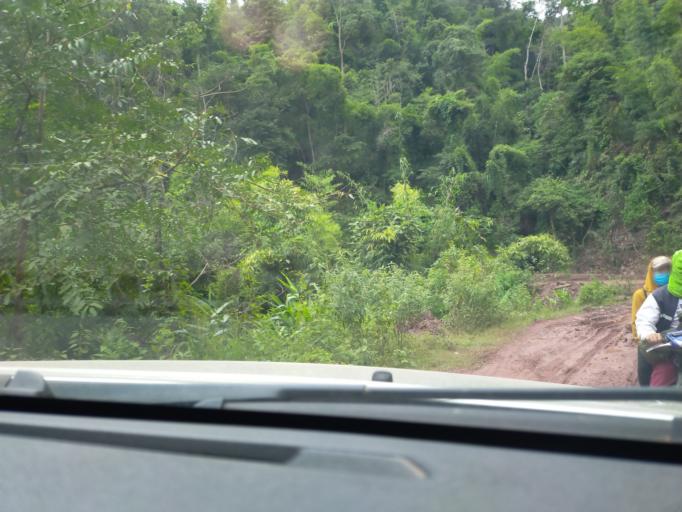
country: TH
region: Nan
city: Chaloem Phra Kiat
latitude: 19.7812
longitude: 101.3612
